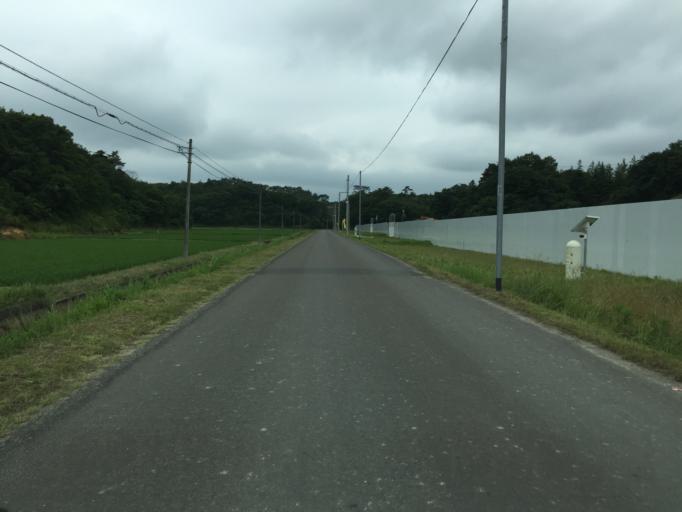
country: JP
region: Fukushima
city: Namie
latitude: 37.7294
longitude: 140.9581
